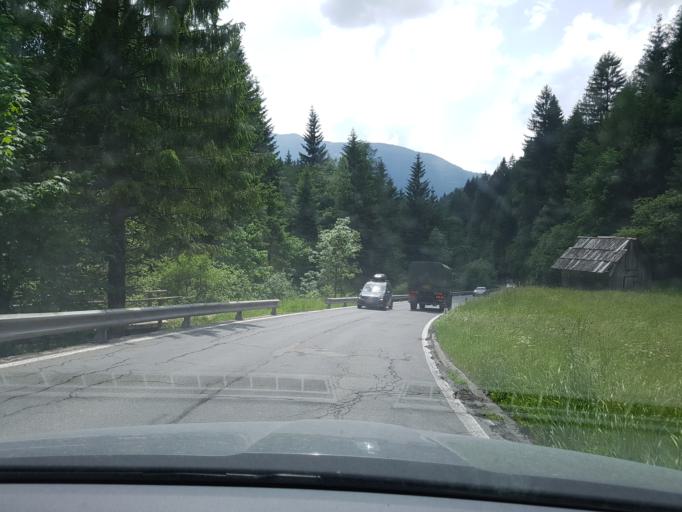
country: AT
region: Carinthia
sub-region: Politischer Bezirk Villach Land
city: Feld am See
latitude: 46.8029
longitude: 13.7564
